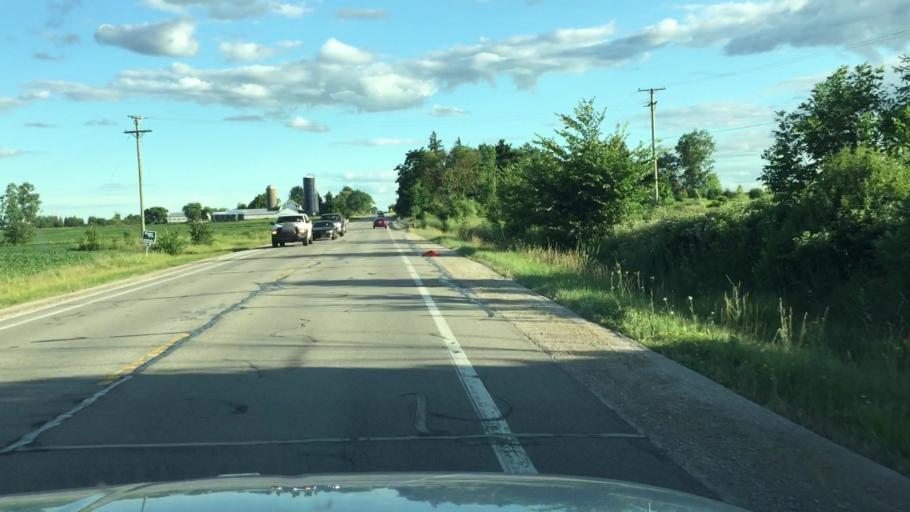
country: US
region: Michigan
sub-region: Saint Clair County
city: Yale
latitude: 43.0946
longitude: -82.7665
